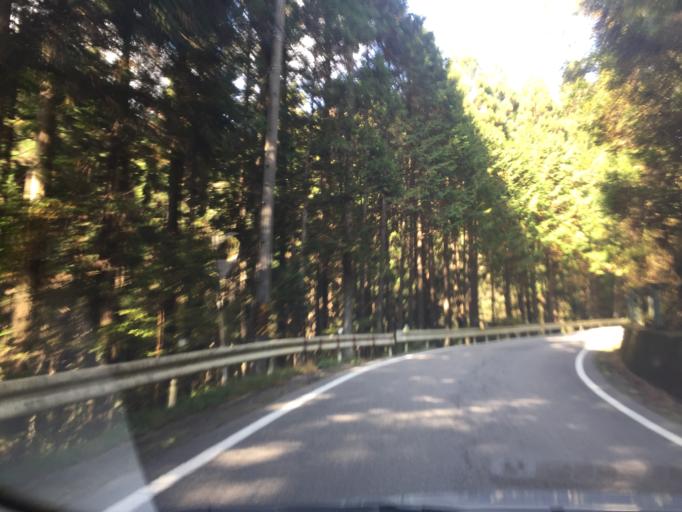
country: JP
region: Aichi
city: Shinshiro
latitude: 35.1438
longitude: 137.6398
